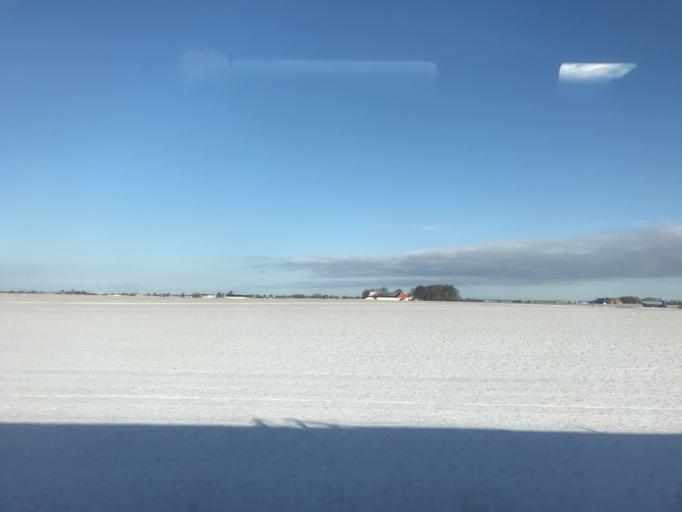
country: SE
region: Skane
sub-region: Staffanstorps Kommun
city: Hjaerup
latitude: 55.6675
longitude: 13.1252
